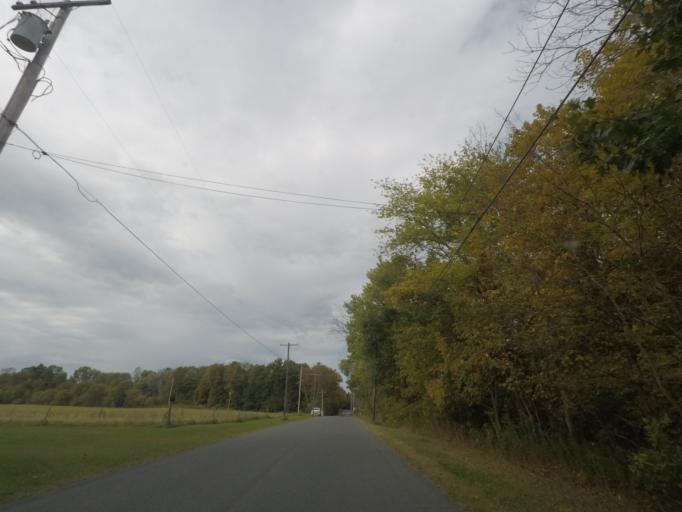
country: US
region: New York
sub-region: Rensselaer County
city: Nassau
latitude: 42.5543
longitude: -73.6250
